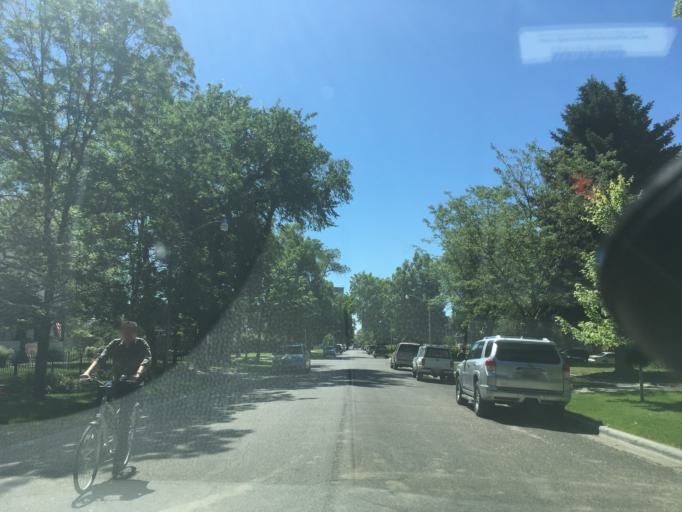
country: US
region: Montana
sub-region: Yellowstone County
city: Billings
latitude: 45.7893
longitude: -108.5183
